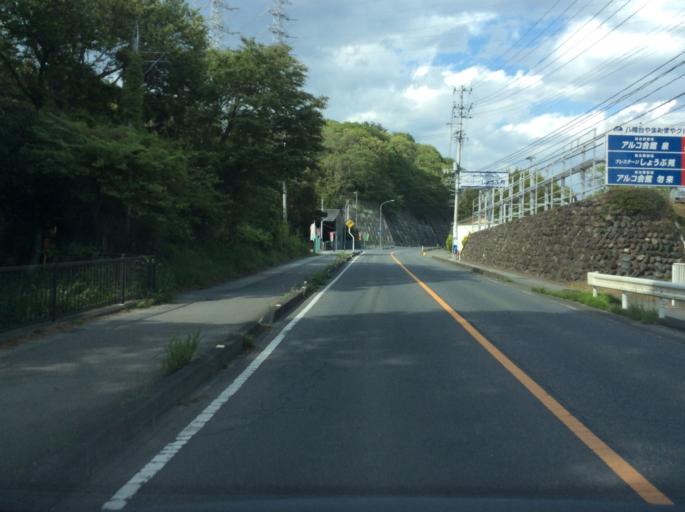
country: JP
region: Fukushima
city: Iwaki
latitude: 36.9228
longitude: 140.8083
